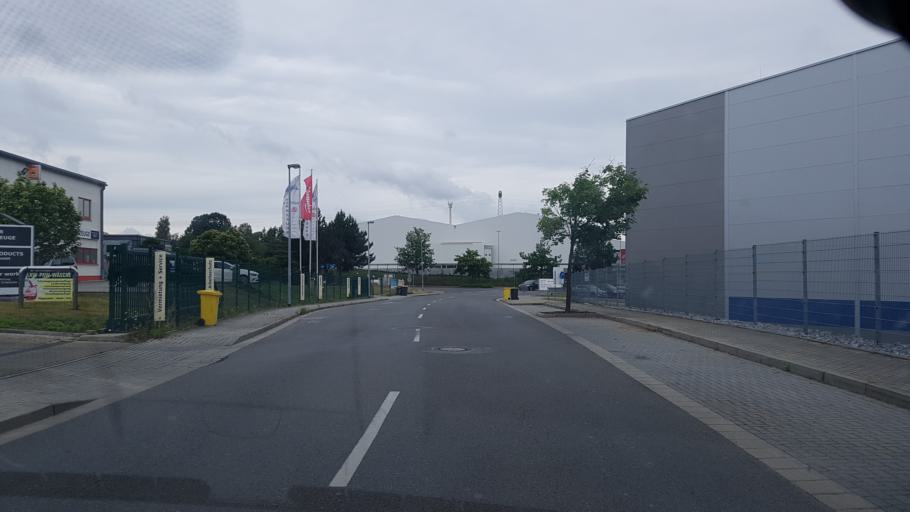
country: DE
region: Saxony
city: Ohorn
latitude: 51.1565
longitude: 14.0496
